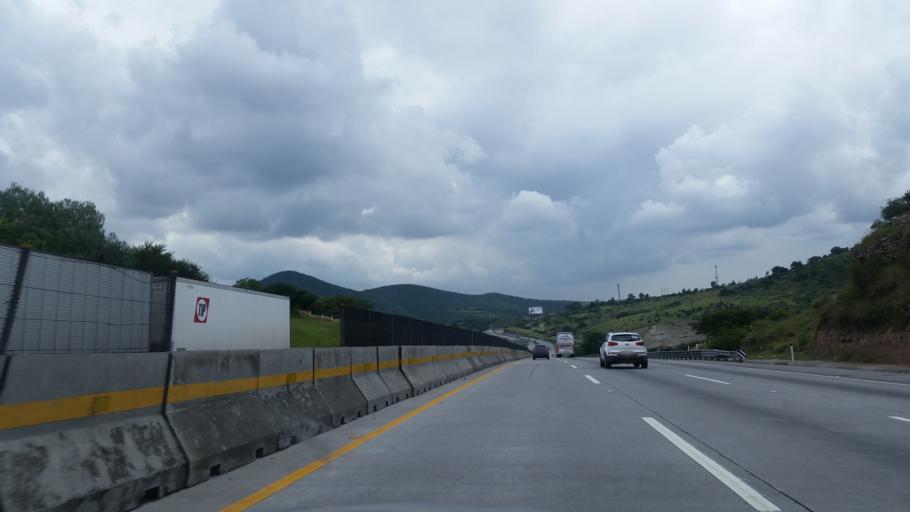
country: MX
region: Hidalgo
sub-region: Tepeji del Rio de Ocampo
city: Santiago Tlautla
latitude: 19.9502
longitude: -99.4017
